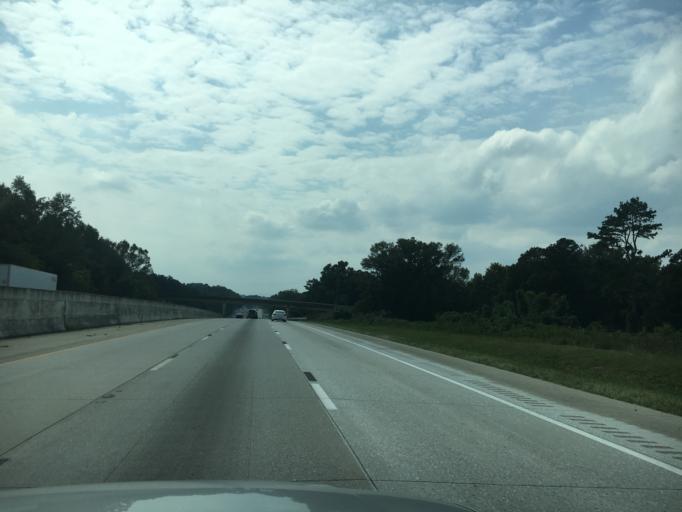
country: US
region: South Carolina
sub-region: Anderson County
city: Northlake
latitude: 34.6037
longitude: -82.6445
